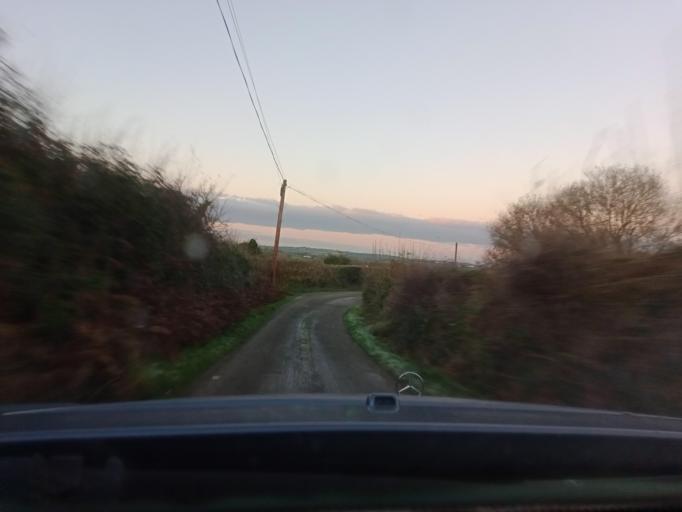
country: IE
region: Leinster
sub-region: Kilkenny
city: Graiguenamanagh
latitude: 52.5857
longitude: -6.9636
